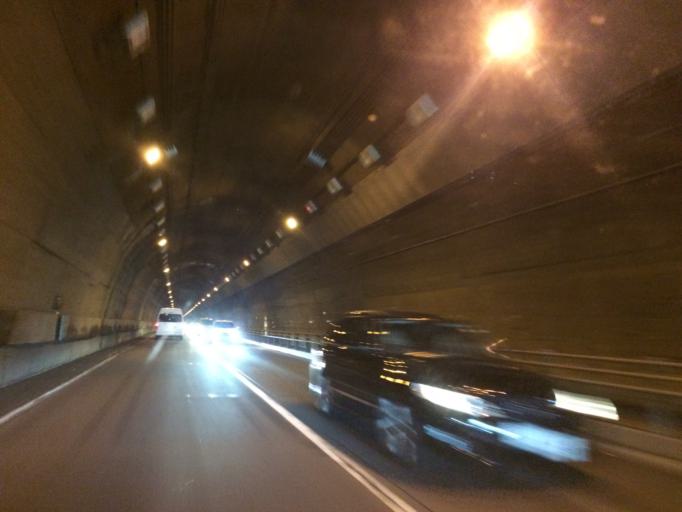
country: JP
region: Hokkaido
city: Otaru
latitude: 43.2102
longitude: 140.9103
